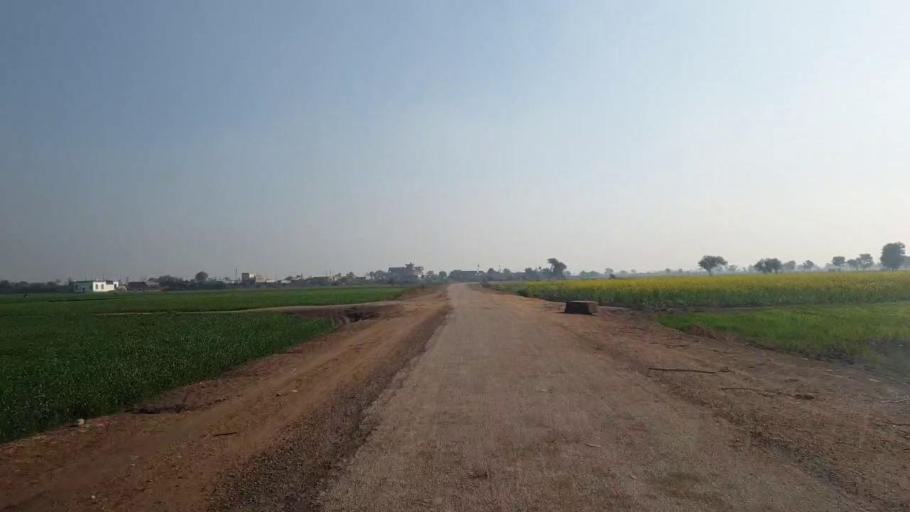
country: PK
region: Sindh
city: Shahdadpur
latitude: 26.0028
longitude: 68.6329
